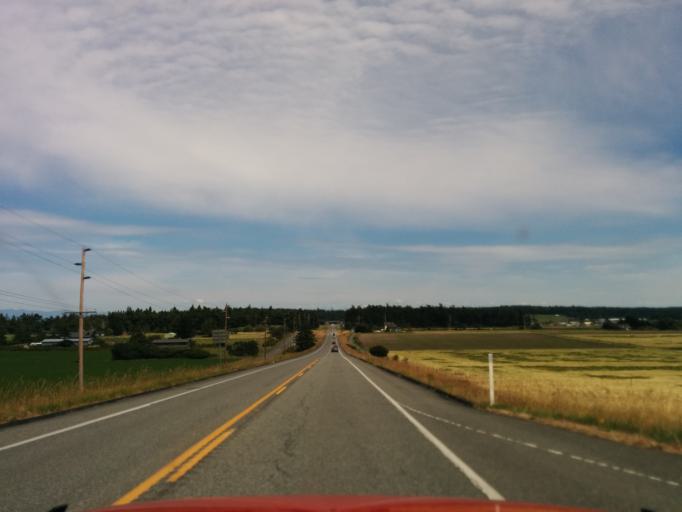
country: US
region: Washington
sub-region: Island County
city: Coupeville
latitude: 48.2123
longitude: -122.7029
